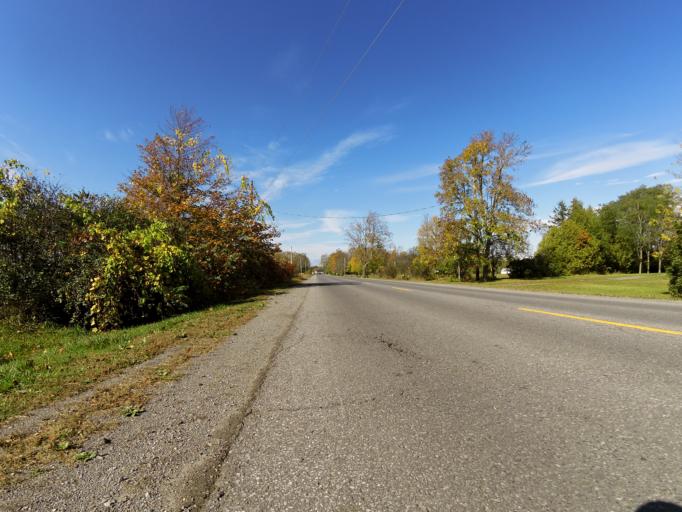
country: CA
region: Ontario
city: Prince Edward
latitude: 44.0153
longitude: -77.3152
